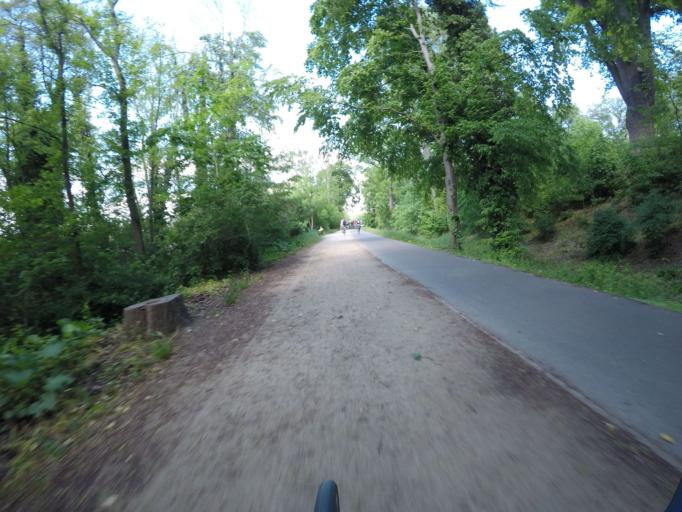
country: DE
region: Brandenburg
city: Potsdam
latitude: 52.4225
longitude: 13.0994
